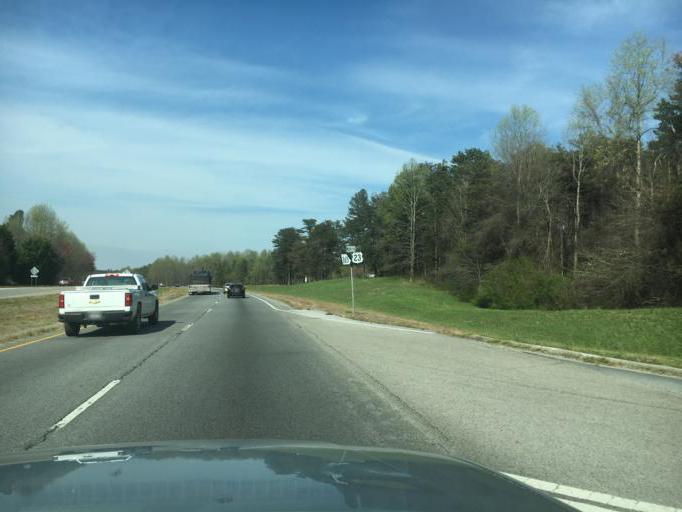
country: US
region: Georgia
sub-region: Habersham County
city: Raoul
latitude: 34.4362
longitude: -83.6313
